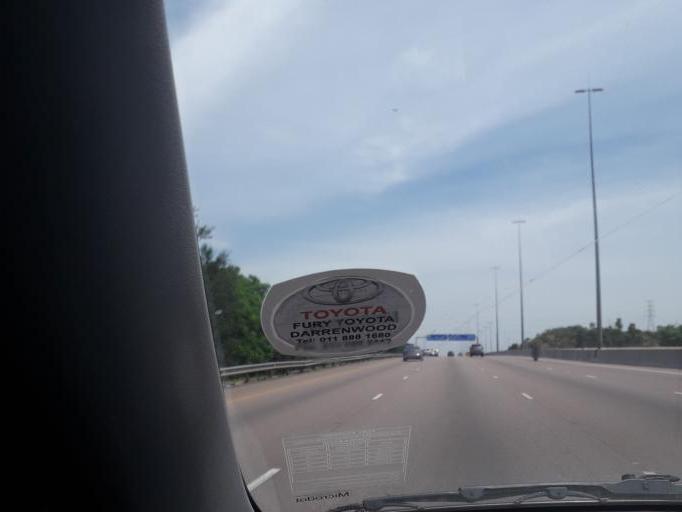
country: ZA
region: Gauteng
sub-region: City of Tshwane Metropolitan Municipality
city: Pretoria
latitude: -25.7302
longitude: 28.2651
